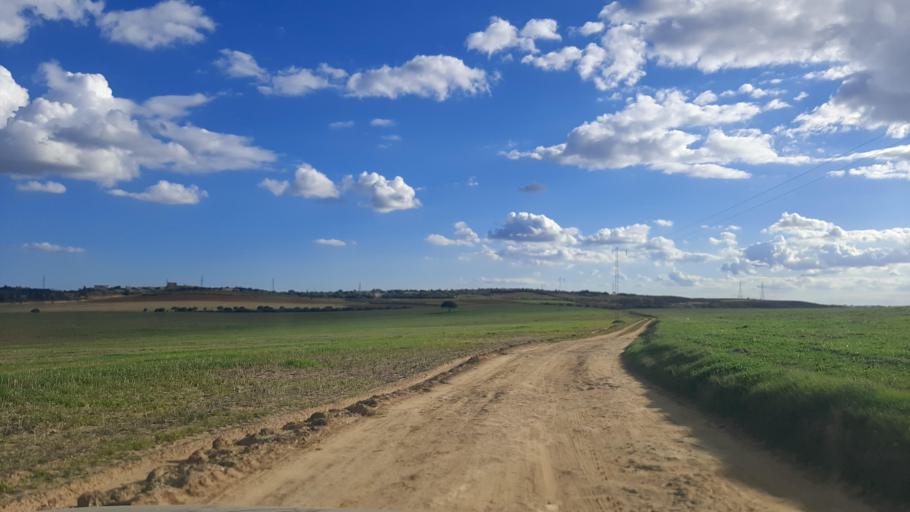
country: TN
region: Nabul
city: Bu `Urqub
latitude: 36.4505
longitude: 10.5011
